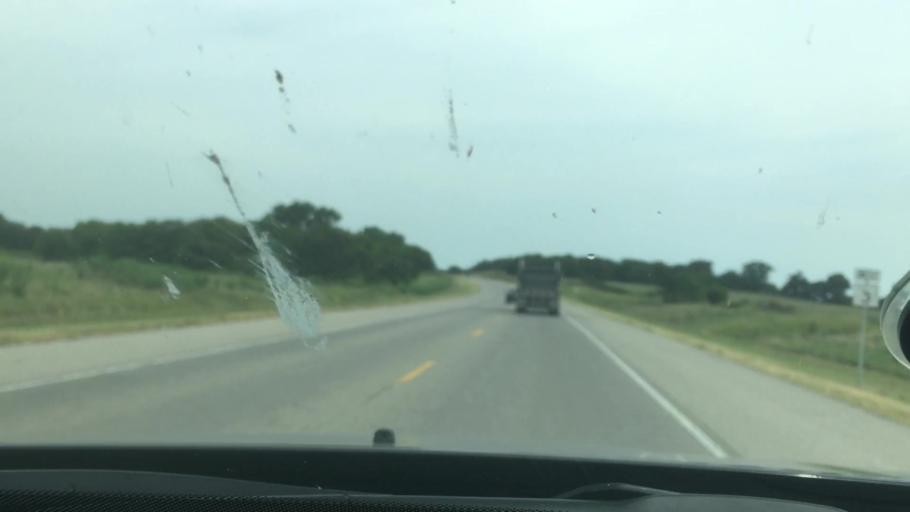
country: US
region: Oklahoma
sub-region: Pontotoc County
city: Ada
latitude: 34.6716
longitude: -96.5700
